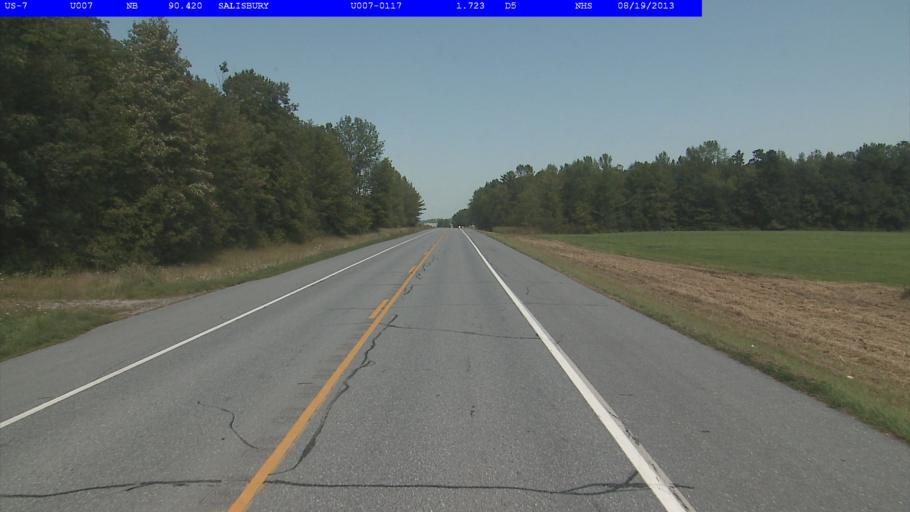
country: US
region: Vermont
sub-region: Addison County
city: Middlebury (village)
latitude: 43.9167
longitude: -73.1115
